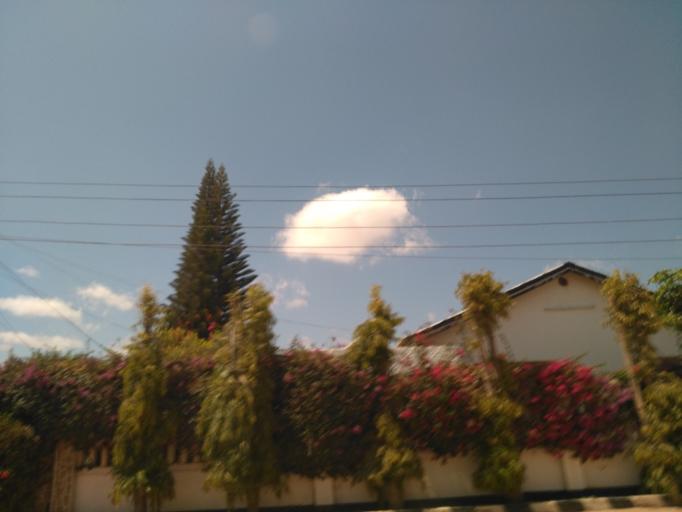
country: TZ
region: Dodoma
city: Kisasa
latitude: -6.1666
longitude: 35.7693
